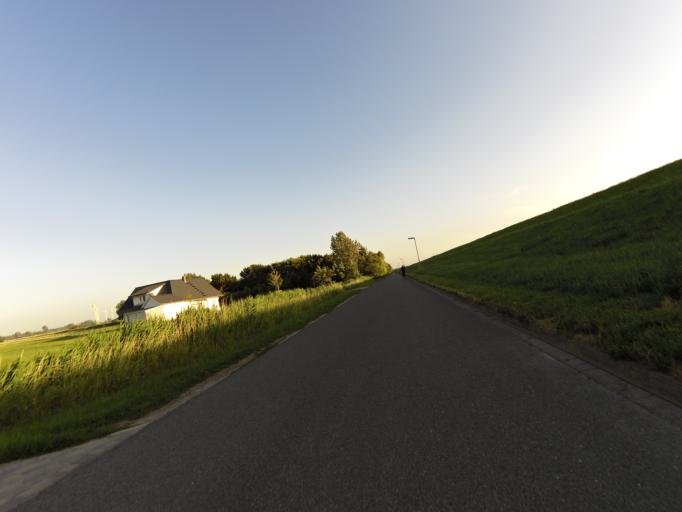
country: DE
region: Lower Saxony
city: Cappel
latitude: 53.7597
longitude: 8.5356
